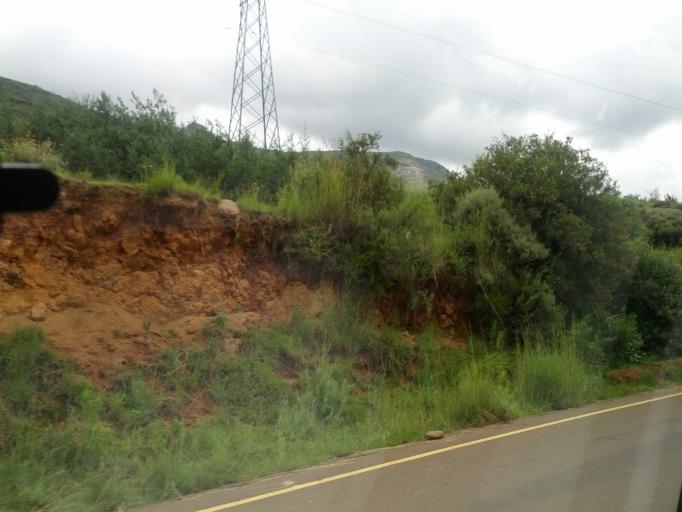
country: LS
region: Butha-Buthe
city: Butha-Buthe
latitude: -29.0502
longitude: 28.3425
